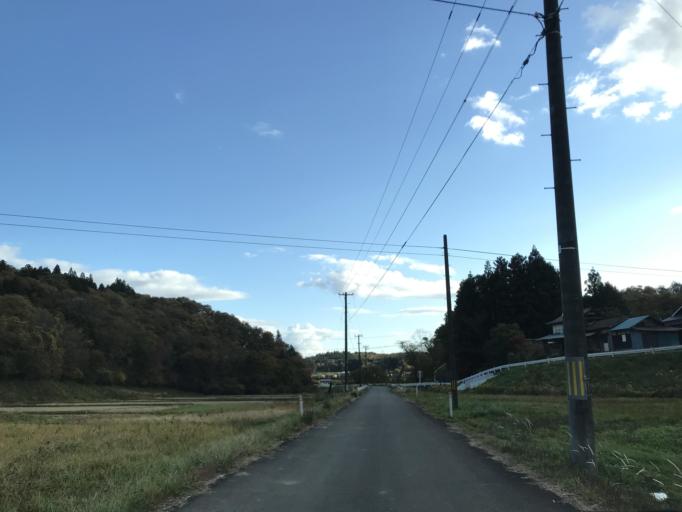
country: JP
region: Iwate
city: Ichinoseki
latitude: 38.8658
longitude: 141.1381
